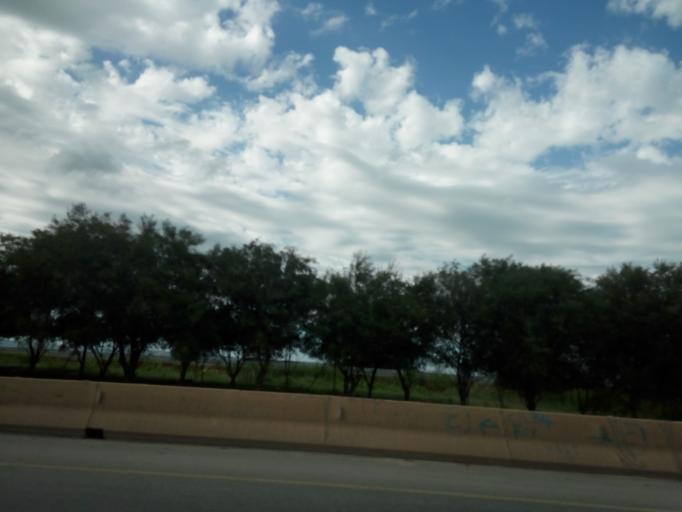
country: DZ
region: Tipaza
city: Mouzaia
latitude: 36.4499
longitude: 2.6675
